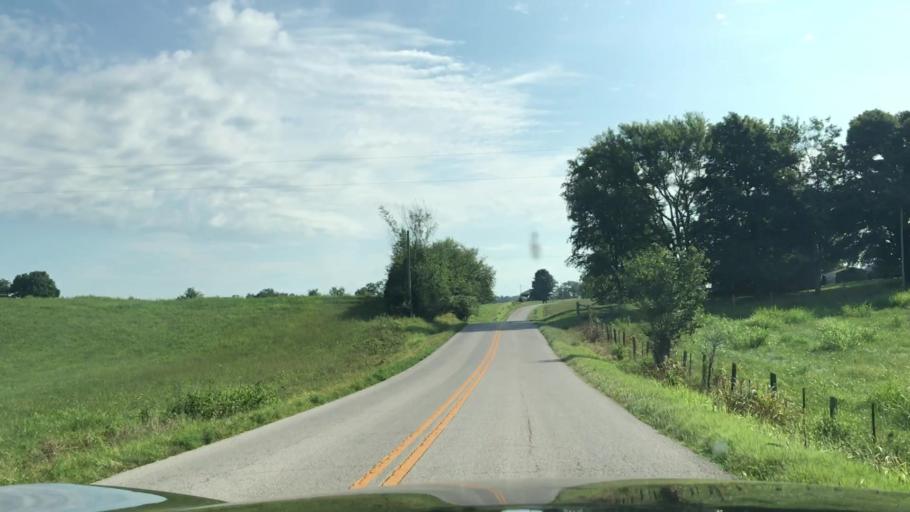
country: US
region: Kentucky
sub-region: Hart County
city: Munfordville
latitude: 37.2248
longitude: -85.7206
